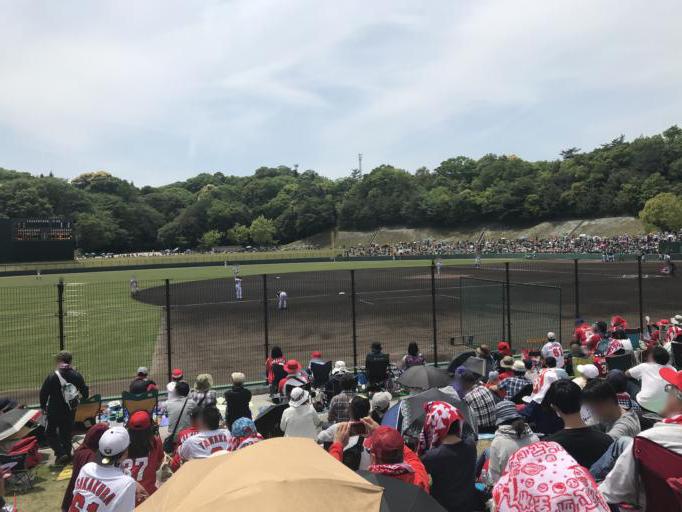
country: JP
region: Yamaguchi
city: Yanai
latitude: 34.0342
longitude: 132.1469
